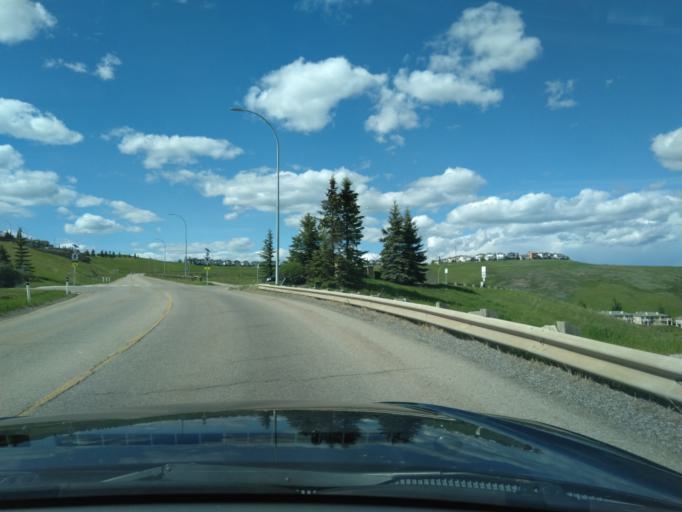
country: CA
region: Alberta
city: Cochrane
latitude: 51.1886
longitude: -114.4251
